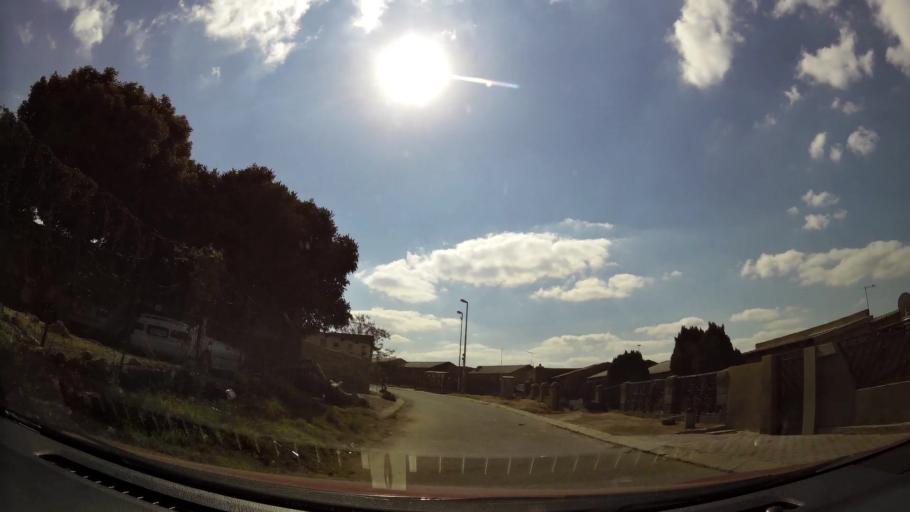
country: ZA
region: Gauteng
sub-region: Ekurhuleni Metropolitan Municipality
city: Tembisa
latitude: -26.0183
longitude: 28.1974
